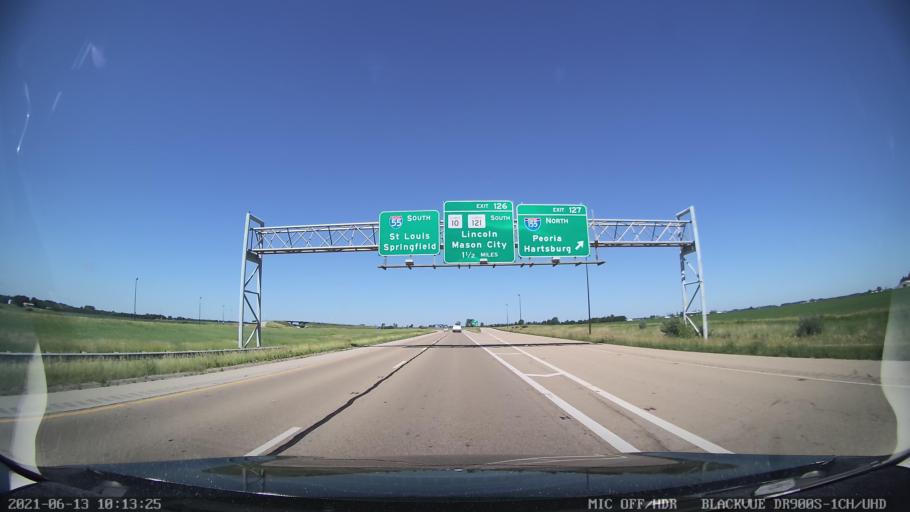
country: US
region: Illinois
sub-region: Logan County
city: Lincoln
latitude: 40.1815
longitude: -89.4057
